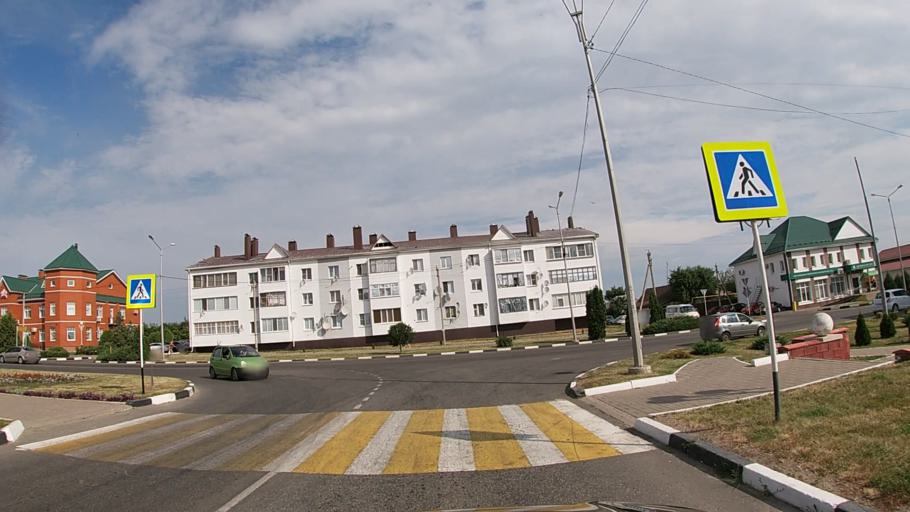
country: RU
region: Belgorod
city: Krasnaya Yaruga
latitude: 50.8023
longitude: 35.6594
